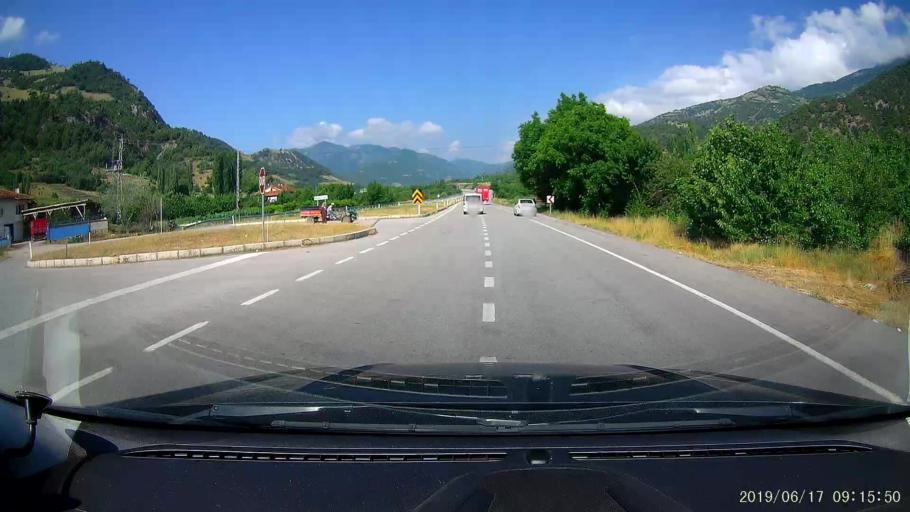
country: TR
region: Amasya
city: Akdag
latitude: 40.7465
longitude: 36.0263
